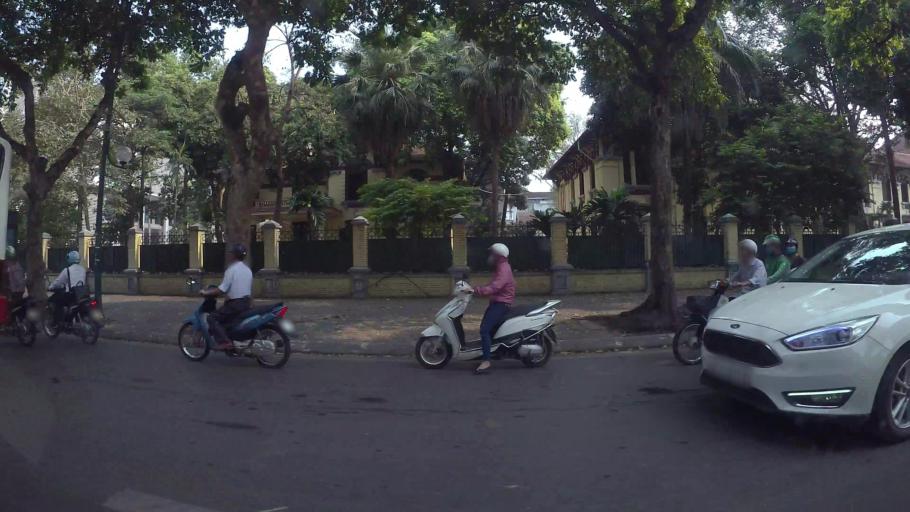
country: VN
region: Ha Noi
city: Hanoi
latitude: 21.0320
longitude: 105.8346
